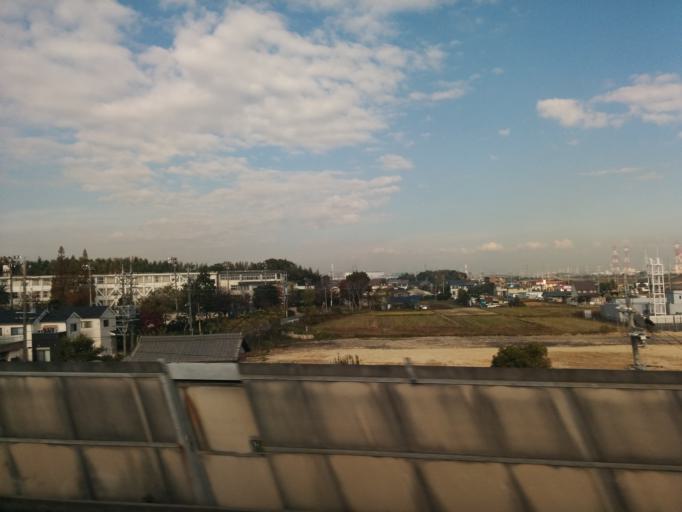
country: JP
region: Aichi
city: Obu
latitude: 35.0231
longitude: 136.9879
